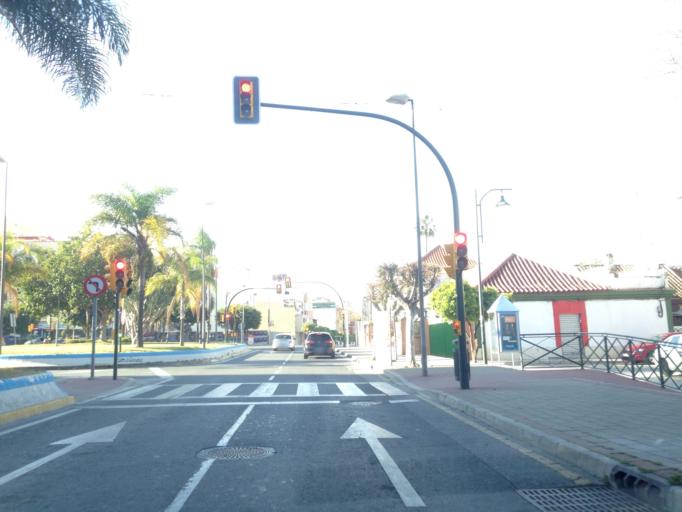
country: ES
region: Andalusia
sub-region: Provincia de Malaga
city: Malaga
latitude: 36.7381
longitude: -4.4229
